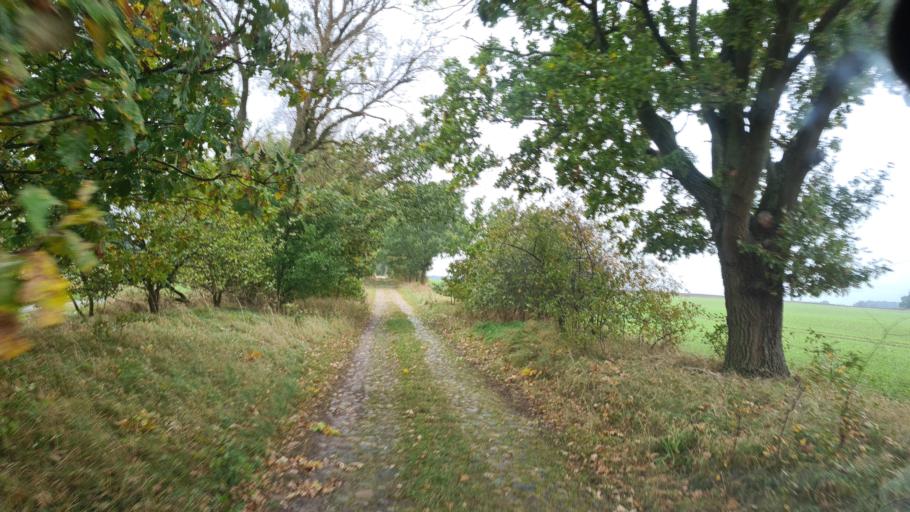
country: DE
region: Brandenburg
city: Furstenwalde
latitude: 52.4211
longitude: 14.0261
